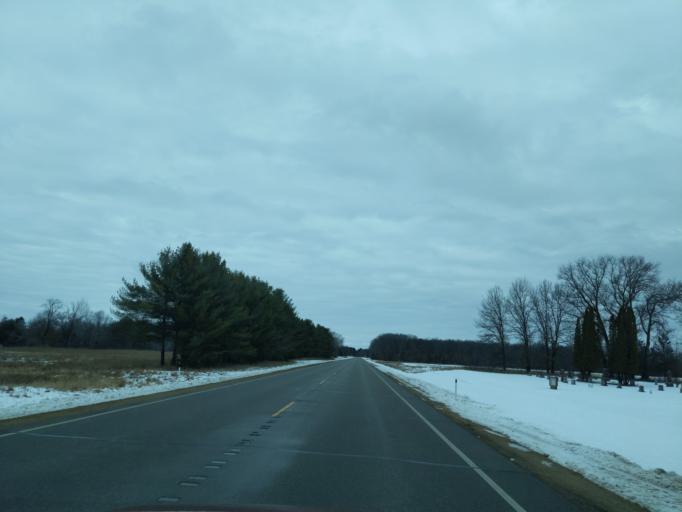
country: US
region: Wisconsin
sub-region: Marquette County
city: Montello
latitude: 43.9269
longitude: -89.3122
